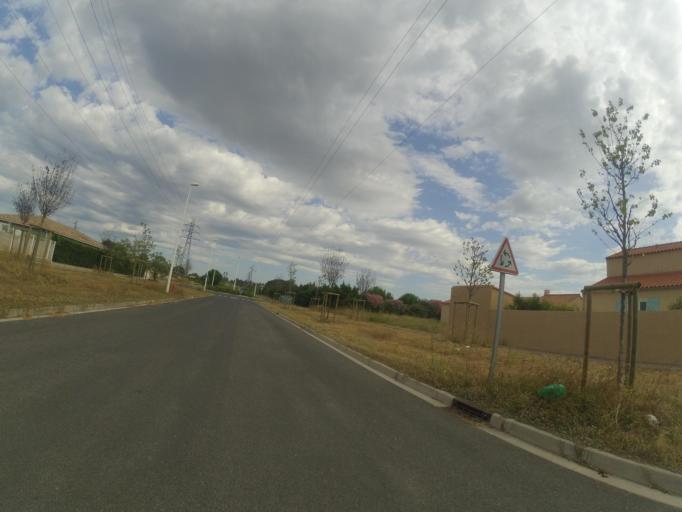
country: FR
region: Languedoc-Roussillon
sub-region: Departement des Pyrenees-Orientales
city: Toulouges
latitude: 42.6718
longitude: 2.8493
